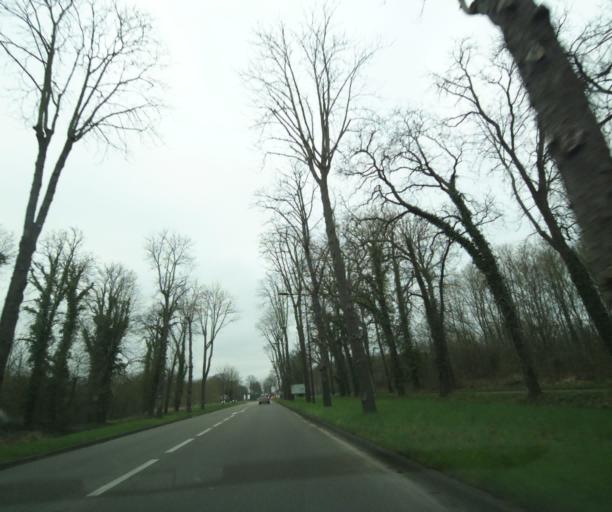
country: FR
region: Ile-de-France
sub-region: Departement des Yvelines
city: Saint-Germain-en-Laye
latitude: 48.9084
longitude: 2.0771
